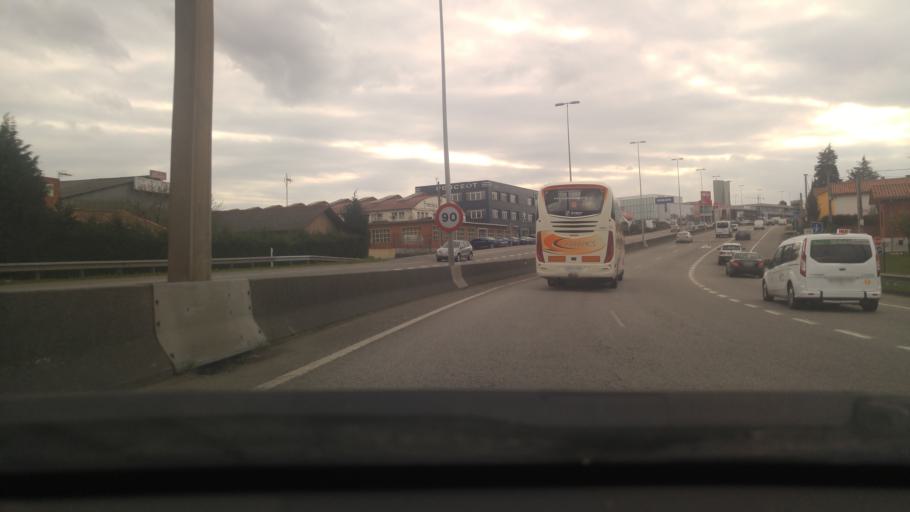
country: ES
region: Asturias
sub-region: Province of Asturias
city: Natahoyo
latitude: 43.5128
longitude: -5.6862
